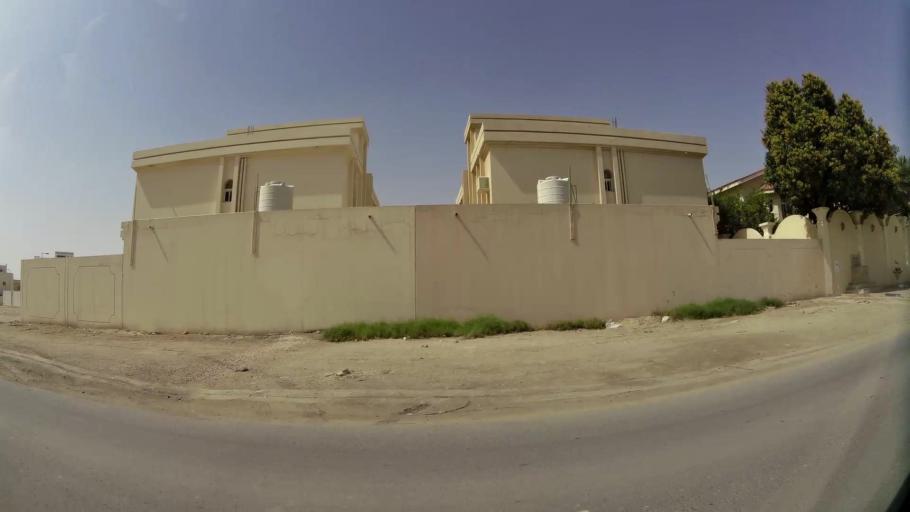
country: QA
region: Baladiyat Umm Salal
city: Umm Salal Muhammad
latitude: 25.3821
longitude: 51.4347
